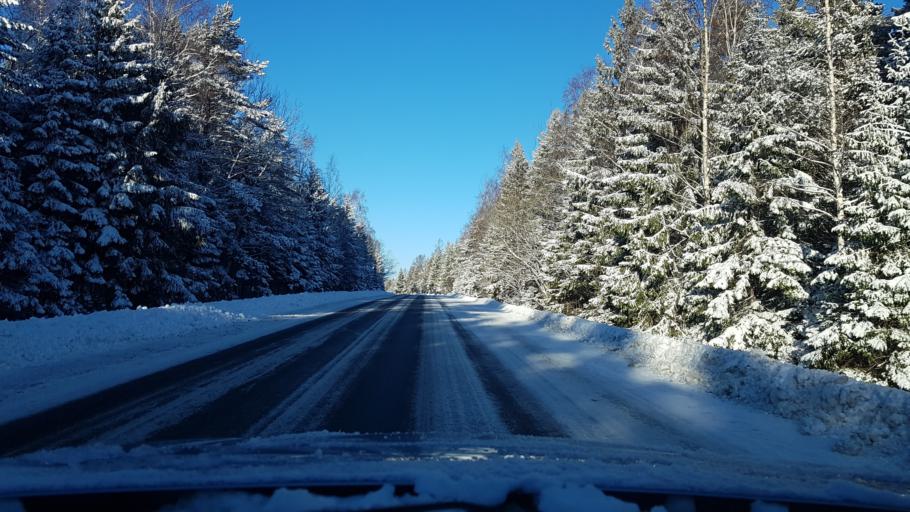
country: EE
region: Hiiumaa
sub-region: Kaerdla linn
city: Kardla
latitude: 58.9740
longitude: 22.8208
